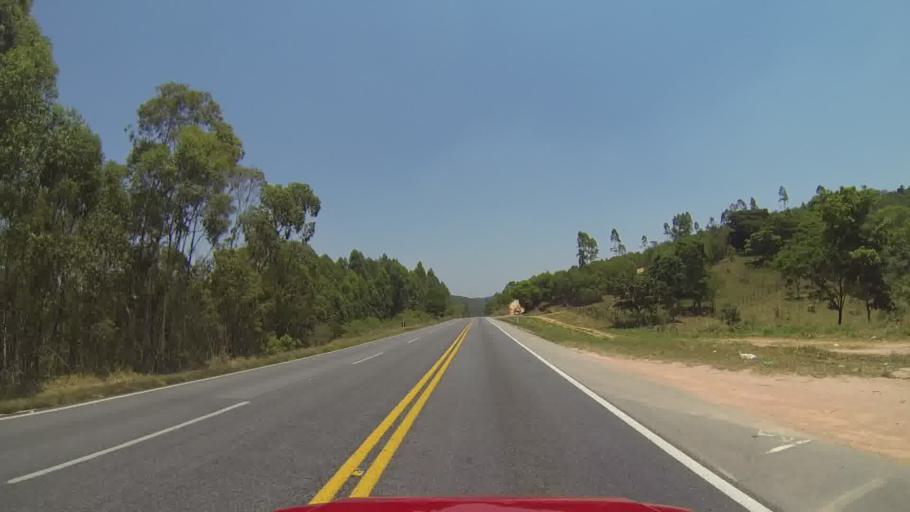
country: BR
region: Minas Gerais
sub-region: Itapecerica
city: Itapecerica
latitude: -20.2810
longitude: -45.1382
